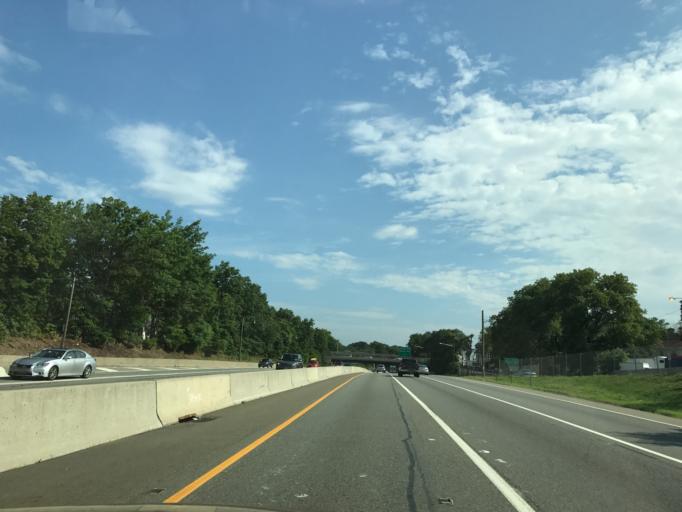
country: US
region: New Jersey
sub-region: Essex County
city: Bloomfield
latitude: 40.7927
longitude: -74.1924
